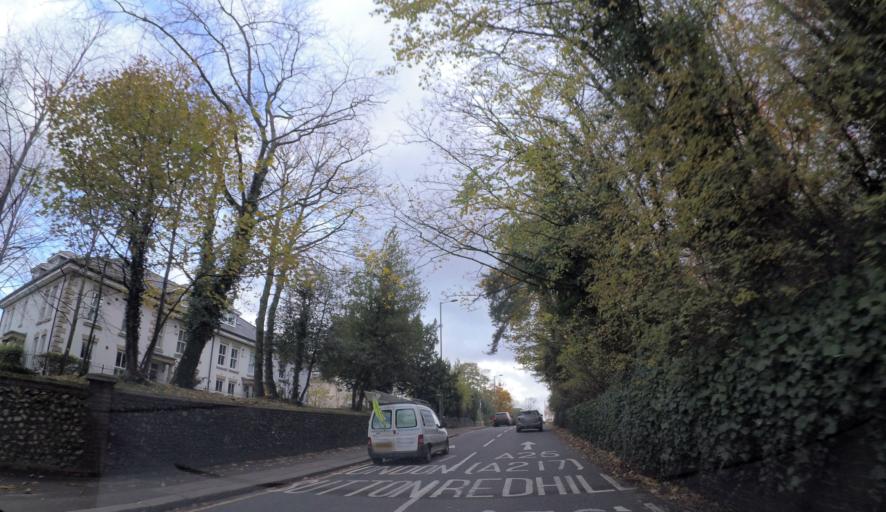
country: GB
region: England
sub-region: Surrey
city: Reigate
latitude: 51.2394
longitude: -0.2088
